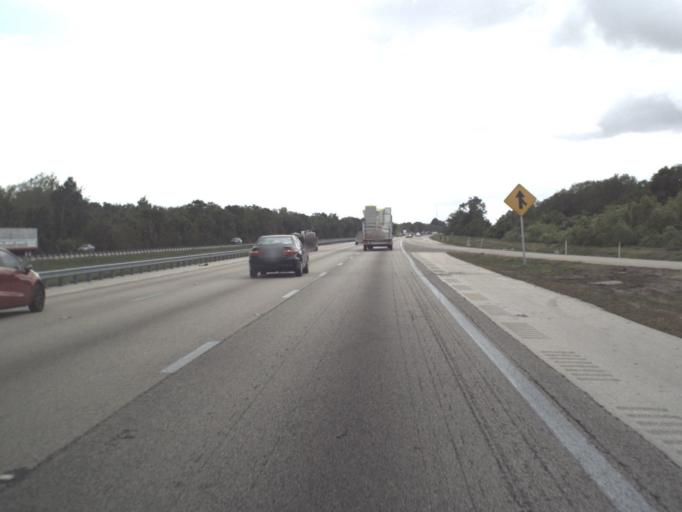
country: US
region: Florida
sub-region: Brevard County
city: South Patrick Shores
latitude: 28.1859
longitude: -80.7065
